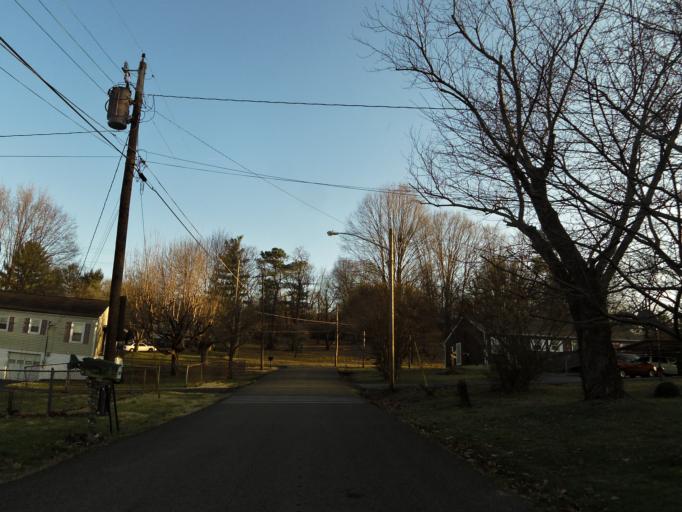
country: US
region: Tennessee
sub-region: Knox County
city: Knoxville
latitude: 36.0160
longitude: -83.8934
